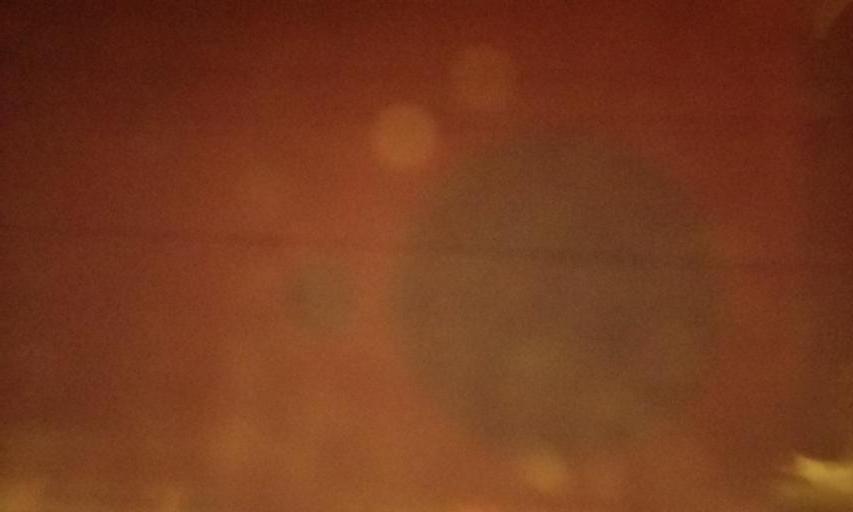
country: JP
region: Okayama
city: Kurashiki
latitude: 34.6202
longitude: 133.7409
